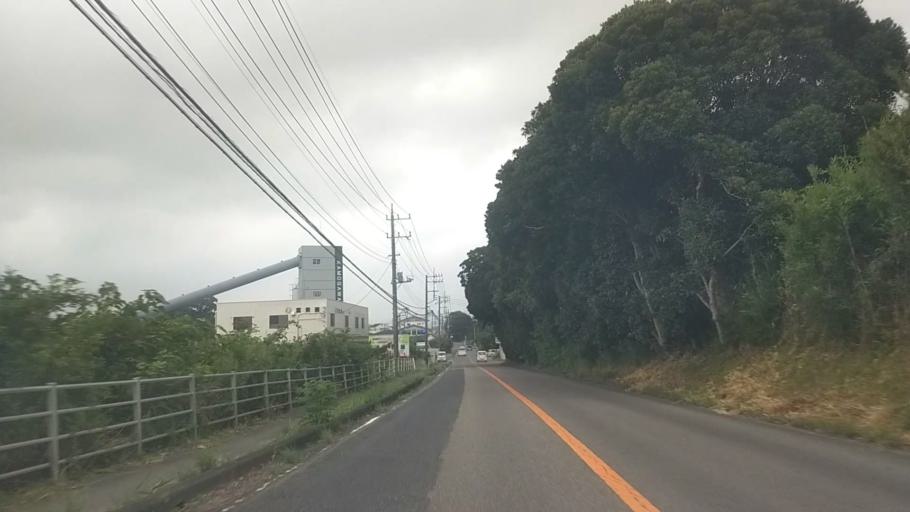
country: JP
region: Chiba
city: Kawaguchi
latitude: 35.1171
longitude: 140.0760
